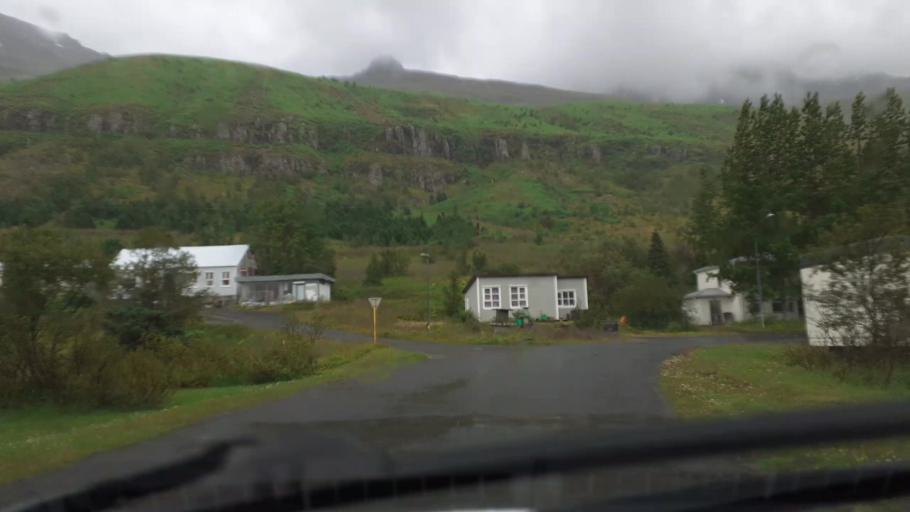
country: IS
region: East
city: Eskifjoerdur
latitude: 65.2629
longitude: -13.9970
